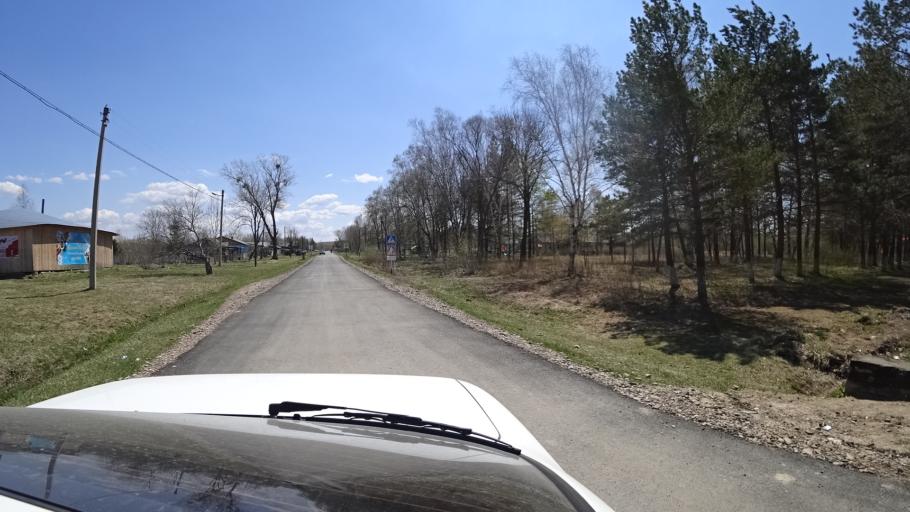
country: RU
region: Primorskiy
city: Dal'nerechensk
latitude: 45.7968
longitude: 133.7675
